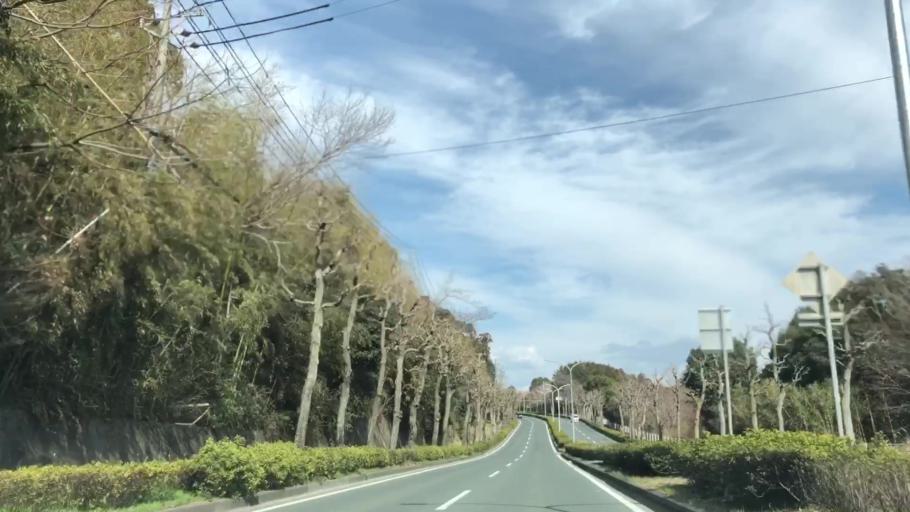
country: JP
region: Shizuoka
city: Hamamatsu
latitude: 34.7473
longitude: 137.6665
